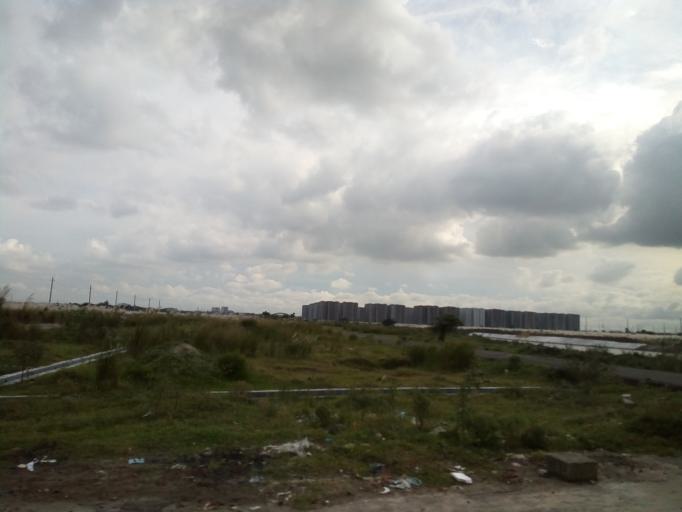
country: BD
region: Dhaka
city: Tungi
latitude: 23.8687
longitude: 90.3608
